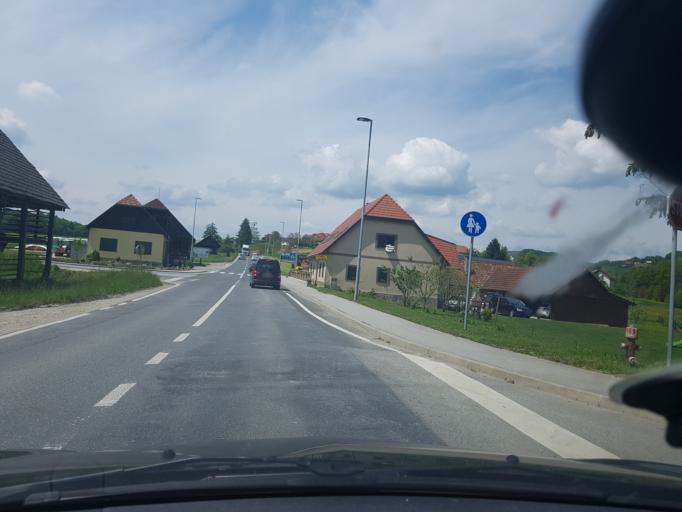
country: SI
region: Smarje pri Jelsah
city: Smarje pri Jelsah
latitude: 46.2303
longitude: 15.5505
